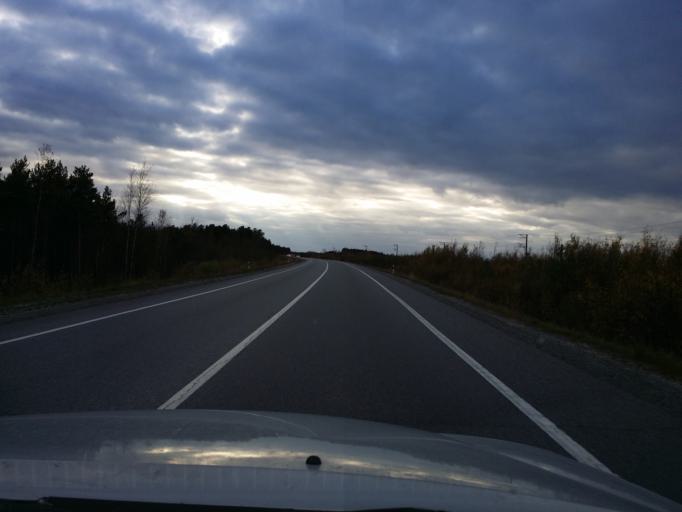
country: RU
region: Khanty-Mansiyskiy Avtonomnyy Okrug
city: Surgut
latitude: 61.4240
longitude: 73.8859
